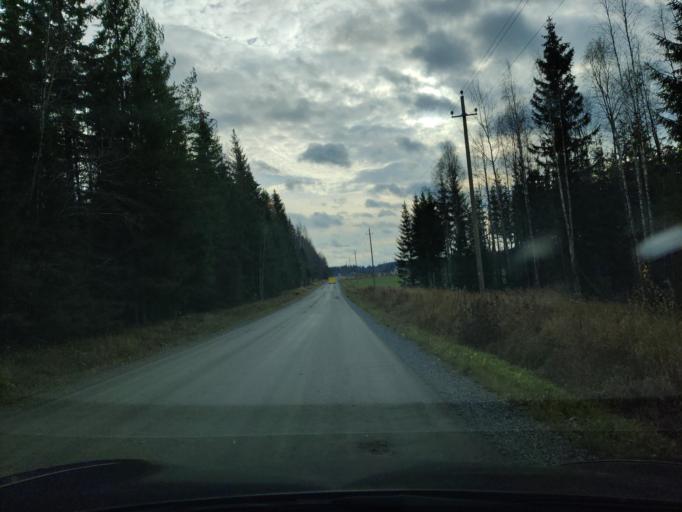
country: FI
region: Northern Savo
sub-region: Kuopio
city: Siilinjaervi
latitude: 63.1102
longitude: 27.5523
